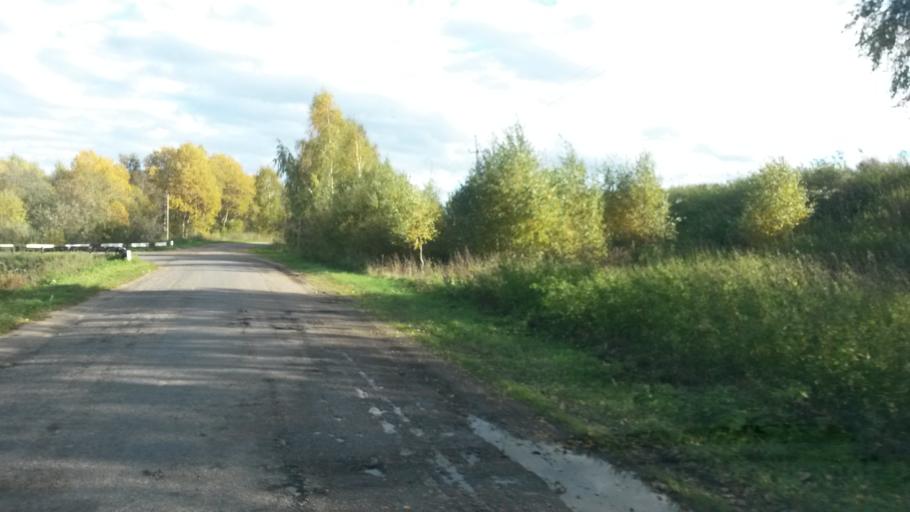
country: RU
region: Jaroslavl
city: Tunoshna
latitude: 57.5245
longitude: 40.0095
